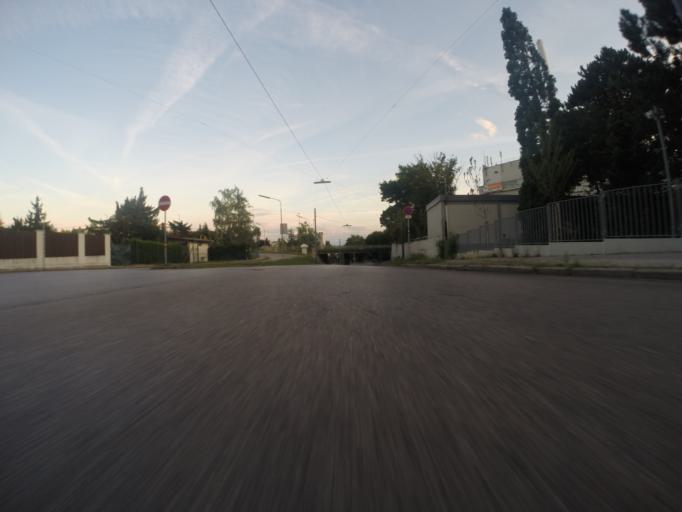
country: AT
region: Vienna
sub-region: Wien Stadt
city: Vienna
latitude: 48.2083
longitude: 16.2908
